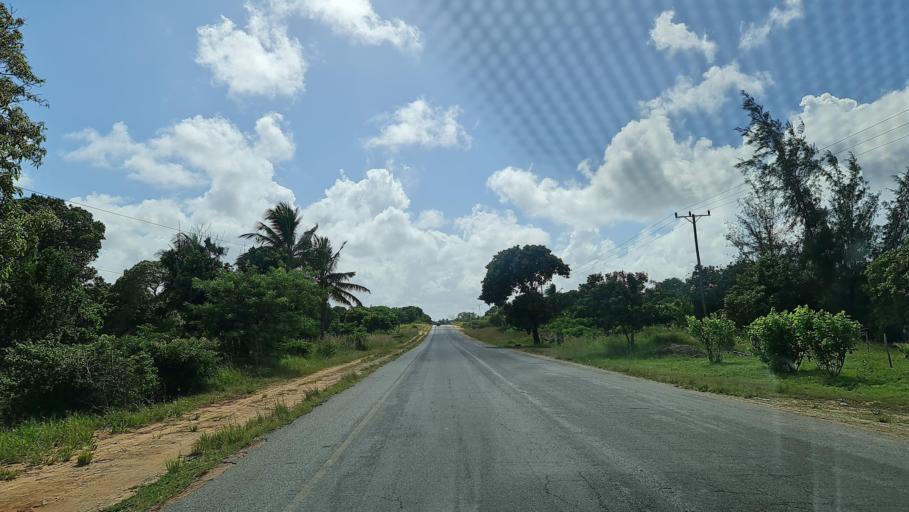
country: MZ
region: Gaza
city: Manjacaze
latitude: -24.6760
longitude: 34.5661
